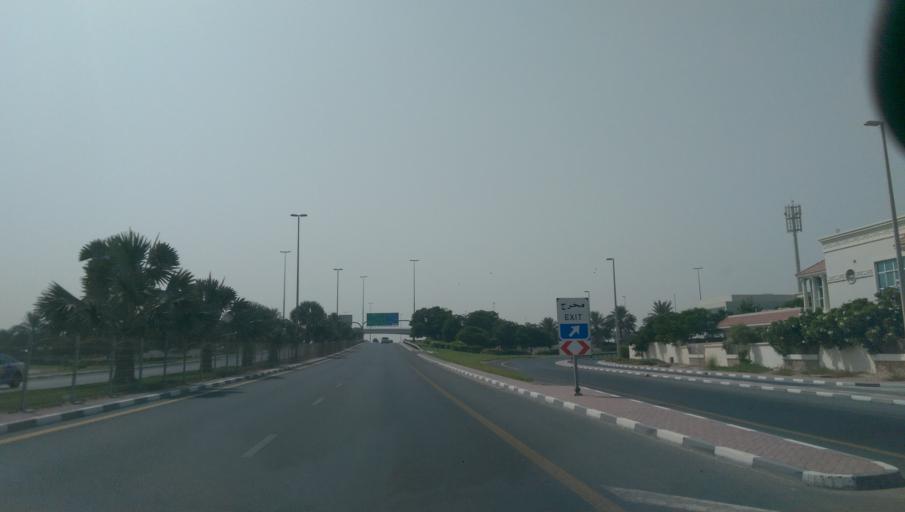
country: AE
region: Dubai
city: Dubai
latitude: 25.1510
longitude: 55.2214
